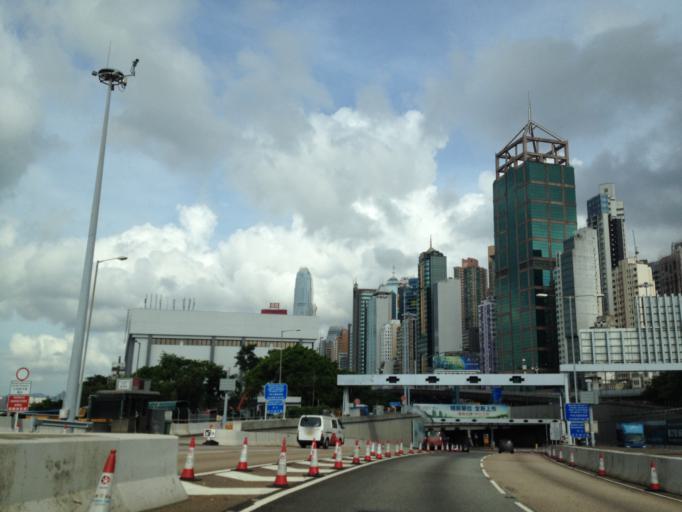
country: HK
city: Hong Kong
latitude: 22.2903
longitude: 114.1416
